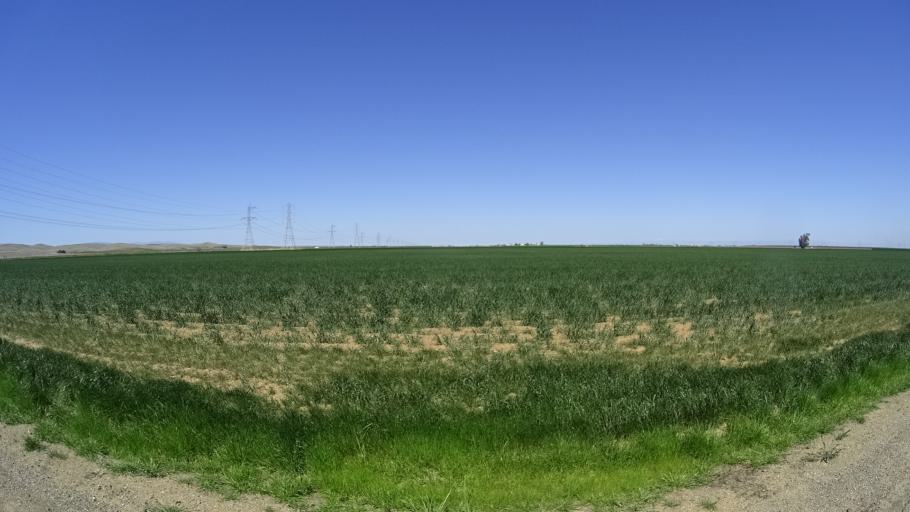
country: US
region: California
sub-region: Glenn County
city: Willows
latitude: 39.4656
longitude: -122.2836
